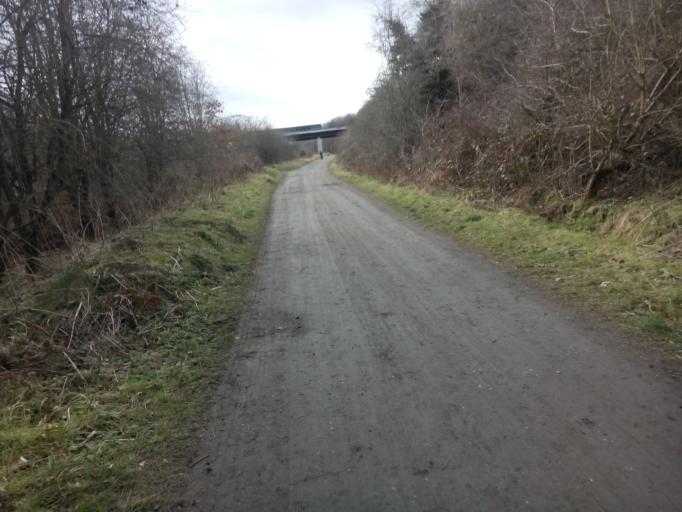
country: GB
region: England
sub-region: County Durham
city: Durham
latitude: 54.7705
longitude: -1.6062
